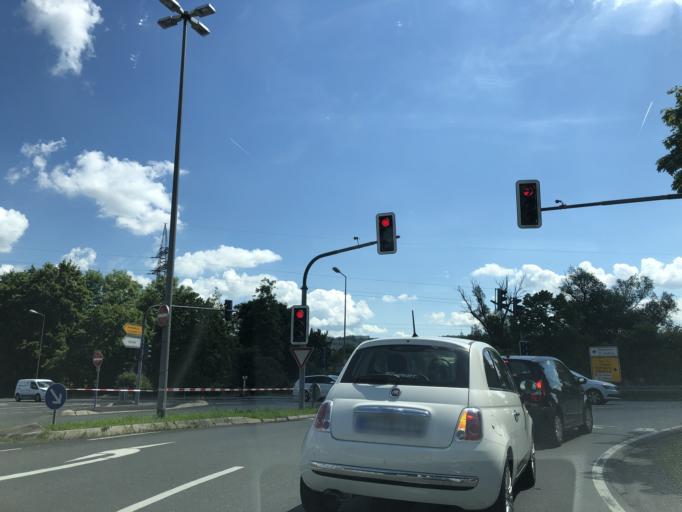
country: DE
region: Hesse
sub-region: Regierungsbezirk Giessen
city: Marburg an der Lahn
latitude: 50.7911
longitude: 8.7517
